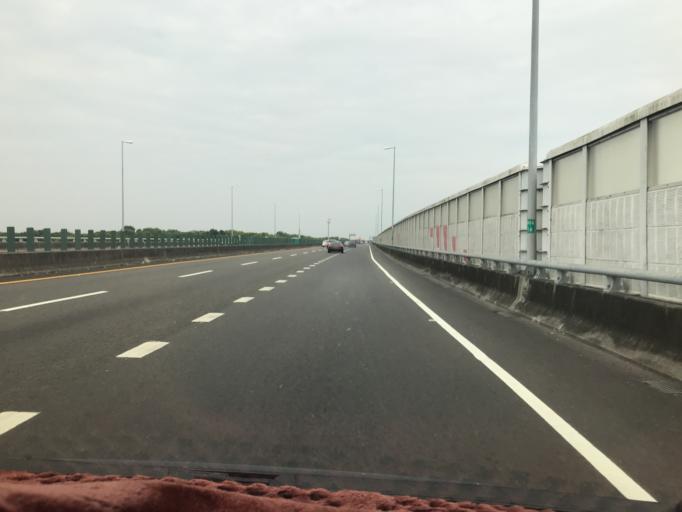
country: TW
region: Taiwan
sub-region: Pingtung
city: Pingtung
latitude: 22.6492
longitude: 120.5446
